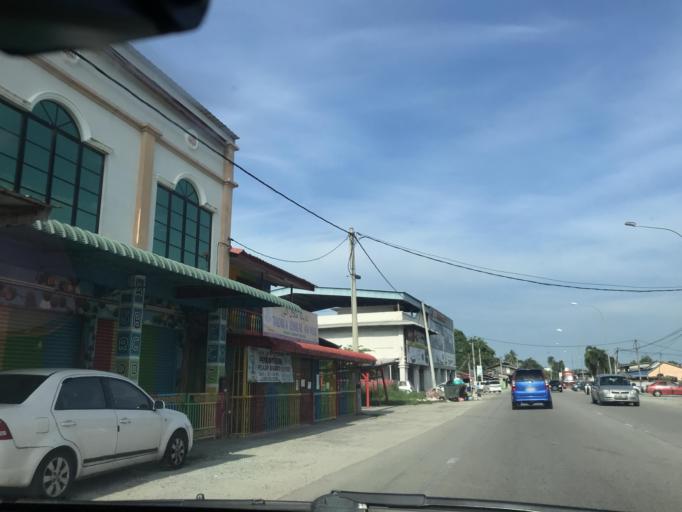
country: MY
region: Kelantan
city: Kota Bharu
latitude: 6.1228
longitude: 102.2815
